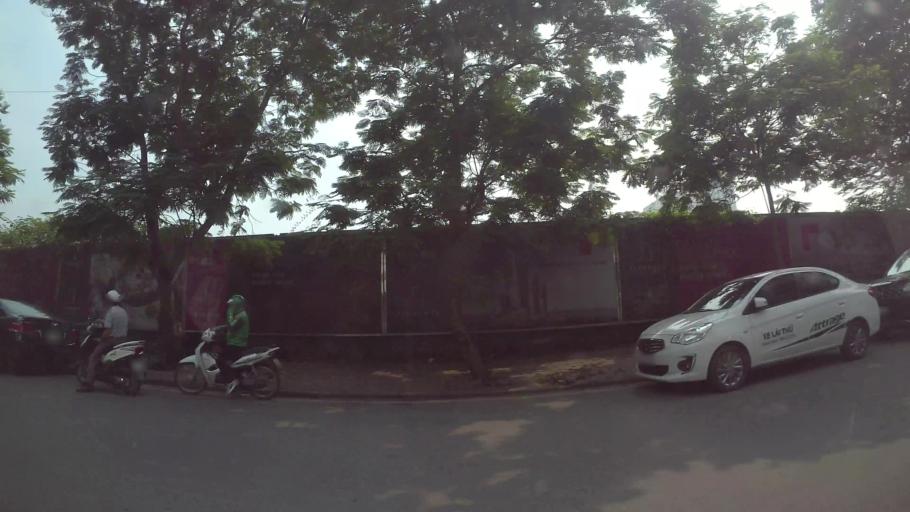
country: VN
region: Ha Noi
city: Dong Da
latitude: 21.0251
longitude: 105.8189
